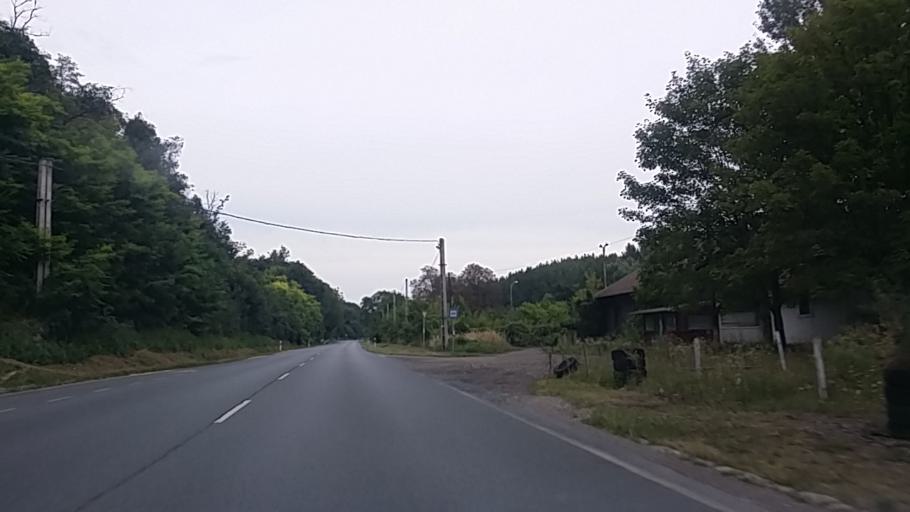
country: HU
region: Tolna
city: Paks
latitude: 46.6411
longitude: 18.8787
